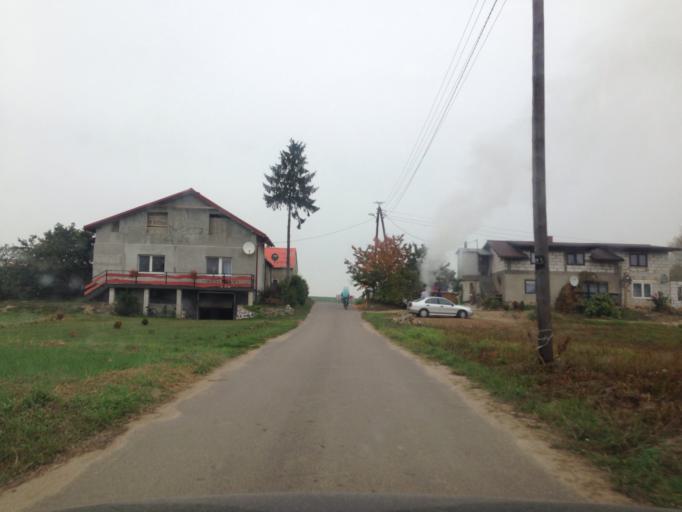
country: PL
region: Kujawsko-Pomorskie
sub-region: Powiat brodnicki
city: Bartniczka
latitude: 53.2540
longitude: 19.5159
